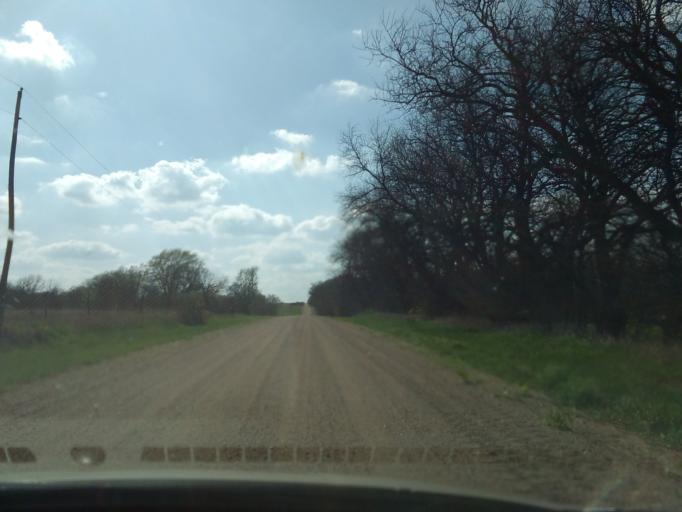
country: US
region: Nebraska
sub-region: Webster County
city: Red Cloud
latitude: 40.0314
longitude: -98.3856
